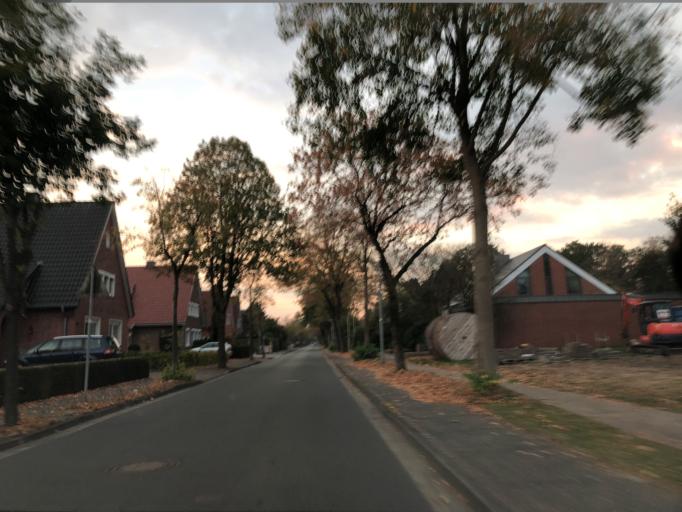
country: DE
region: Lower Saxony
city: Papenburg
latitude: 53.0741
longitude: 7.4098
